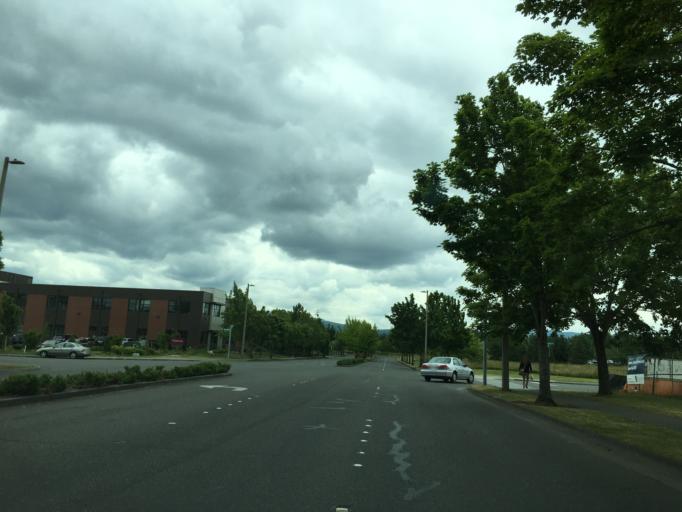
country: US
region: Washington
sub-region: Whatcom County
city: Bellingham
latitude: 48.7997
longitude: -122.4961
